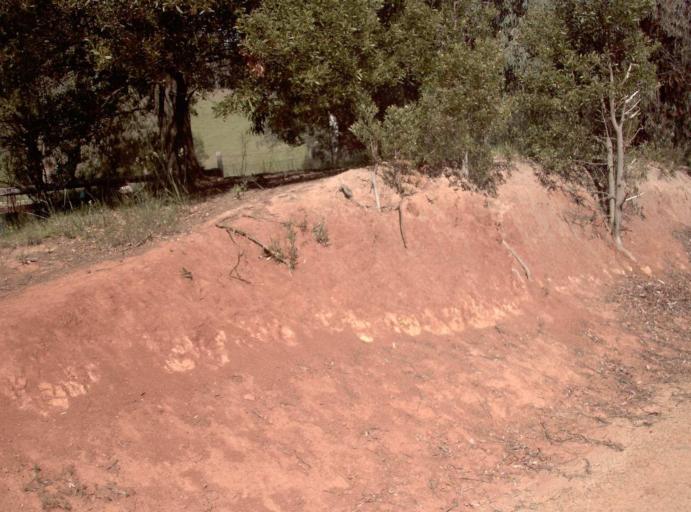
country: AU
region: New South Wales
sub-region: Bombala
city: Bombala
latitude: -37.1710
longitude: 148.7208
